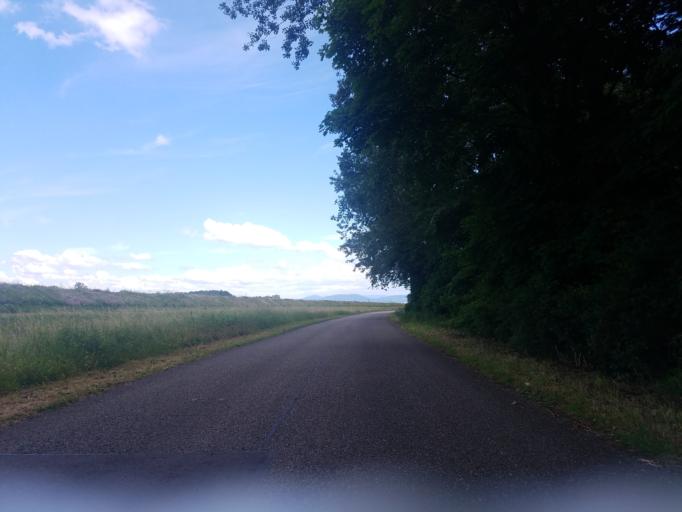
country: DE
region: Baden-Wuerttemberg
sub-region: Karlsruhe Region
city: Greffern
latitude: 48.7595
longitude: 7.9839
